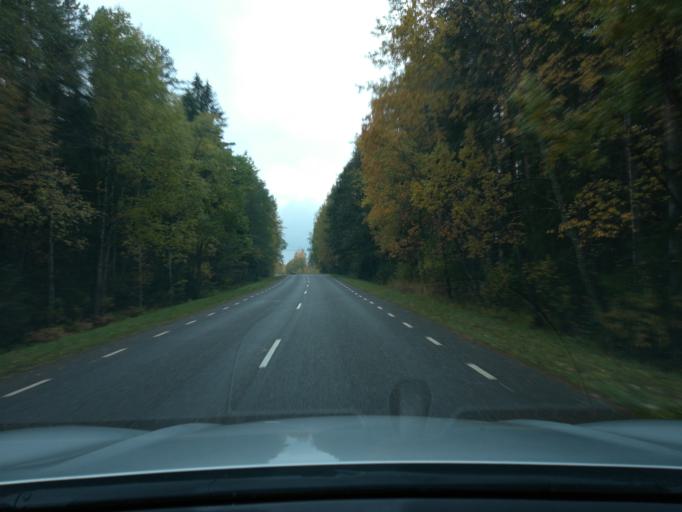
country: EE
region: Ida-Virumaa
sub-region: Johvi vald
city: Johvi
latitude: 59.0798
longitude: 27.3293
